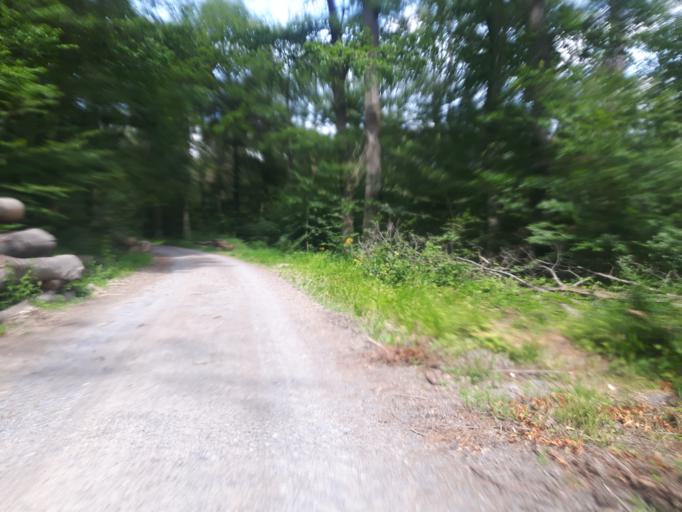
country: DE
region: Baden-Wuerttemberg
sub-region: Regierungsbezirk Stuttgart
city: Guglingen
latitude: 49.0343
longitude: 9.0037
